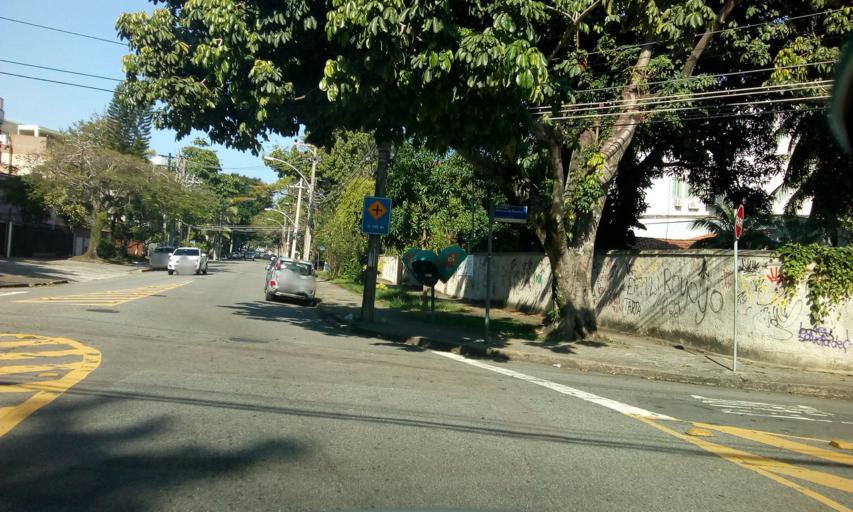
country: BR
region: Rio de Janeiro
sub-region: Rio De Janeiro
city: Rio de Janeiro
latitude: -23.0116
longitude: -43.3130
